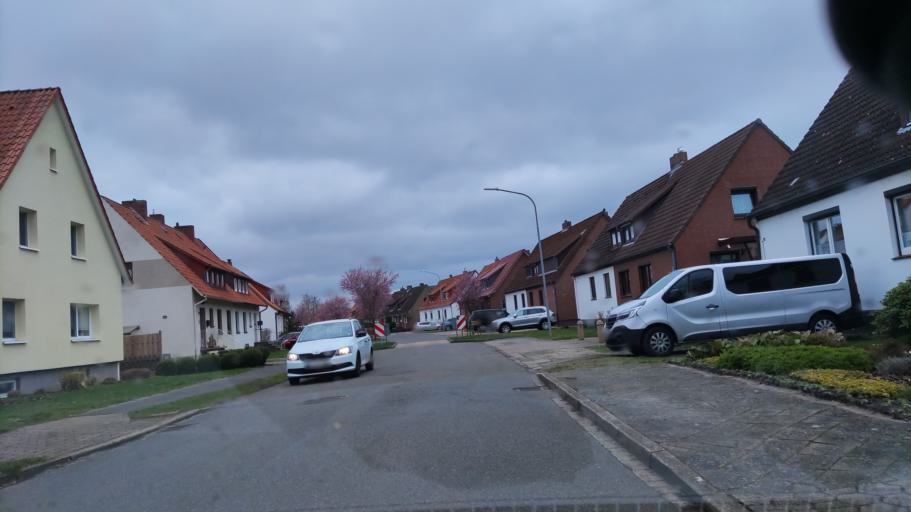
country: DE
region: Lower Saxony
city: Winsen
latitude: 53.3603
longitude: 10.2198
